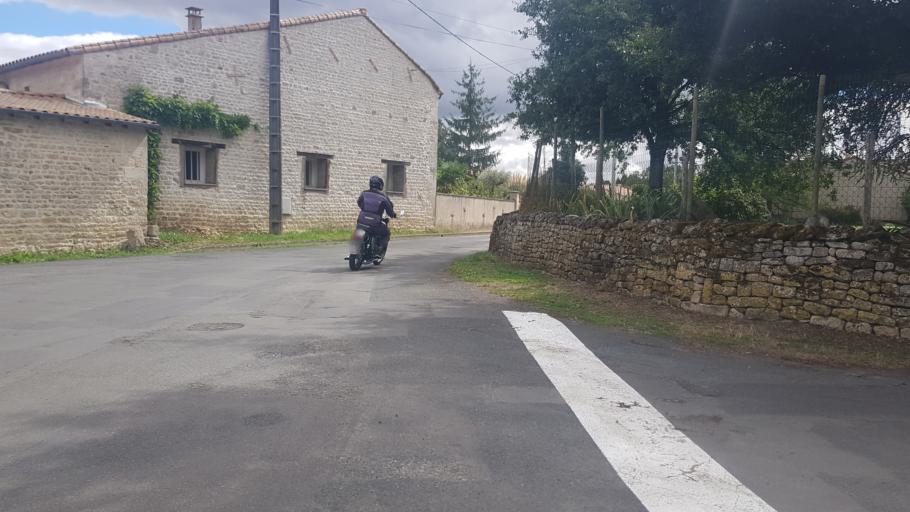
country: FR
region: Poitou-Charentes
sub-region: Departement des Deux-Sevres
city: Vouille
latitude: 46.3272
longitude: -0.3430
